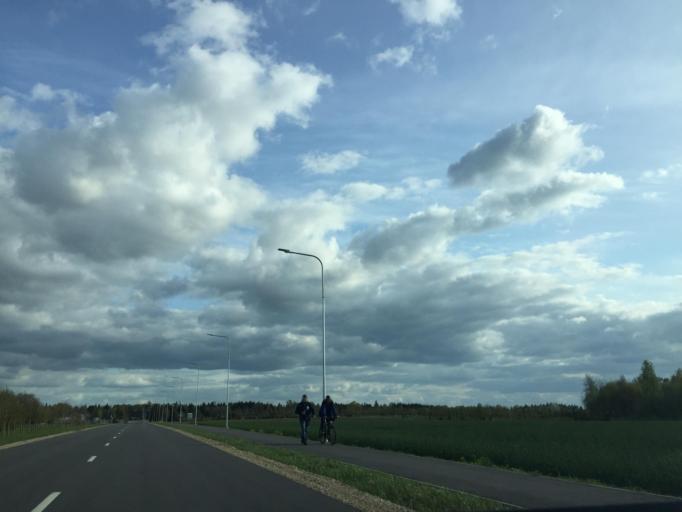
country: LV
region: Sigulda
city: Sigulda
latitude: 57.1371
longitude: 24.8617
